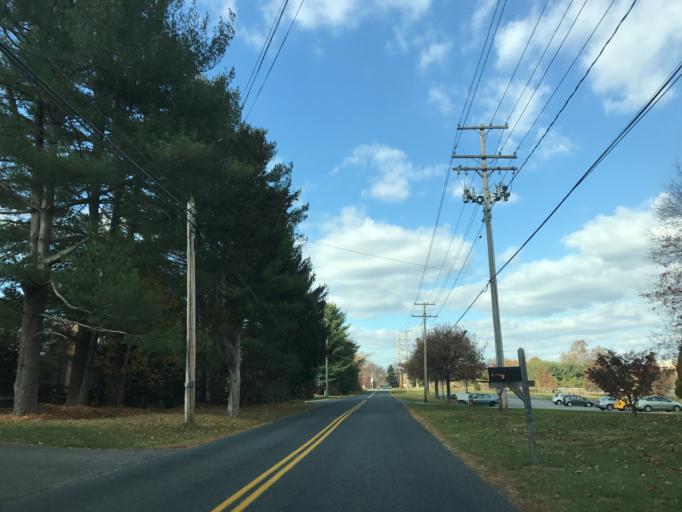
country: US
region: Maryland
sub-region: Harford County
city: Fallston
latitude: 39.5175
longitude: -76.4134
